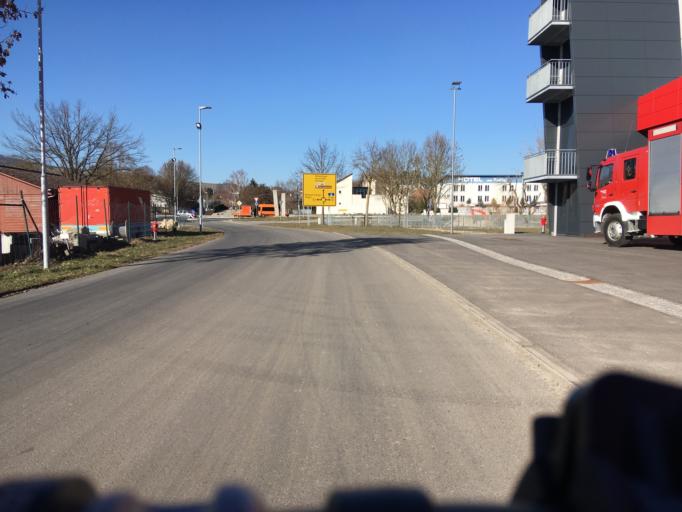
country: DE
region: Baden-Wuerttemberg
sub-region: Freiburg Region
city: Hilzingen
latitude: 47.7612
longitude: 8.7775
